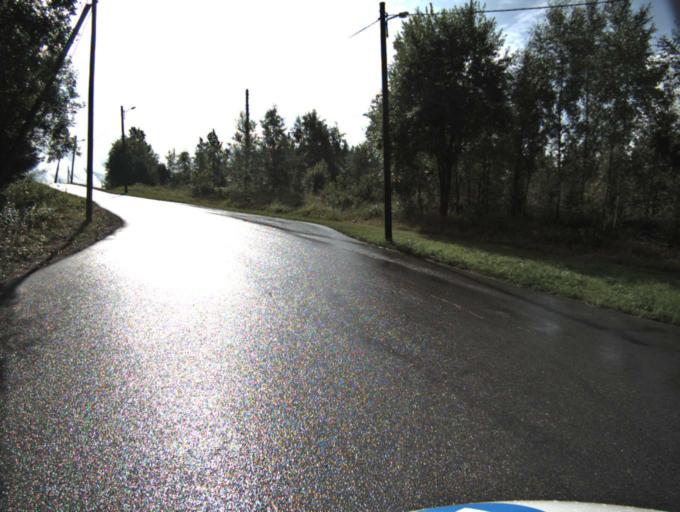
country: SE
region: Vaestra Goetaland
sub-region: Ulricehamns Kommun
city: Ulricehamn
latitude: 57.7298
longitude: 13.3076
